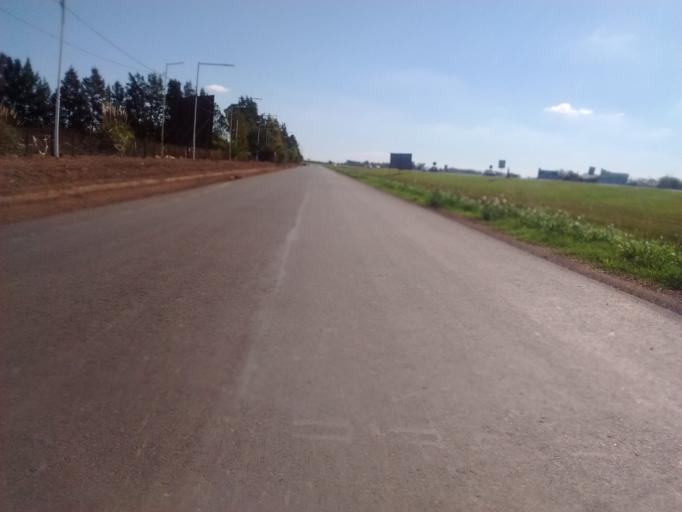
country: AR
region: Santa Fe
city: Roldan
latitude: -32.9296
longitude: -60.8802
